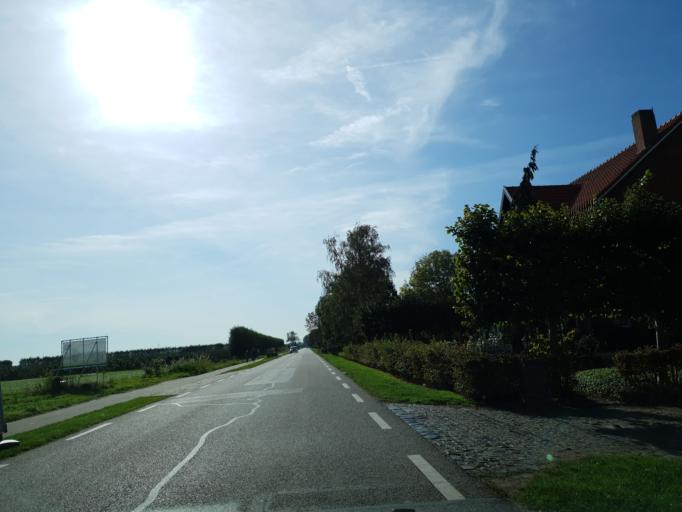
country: NL
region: North Brabant
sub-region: Gemeente Woensdrecht
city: Woensdrecht
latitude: 51.3880
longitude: 4.3144
